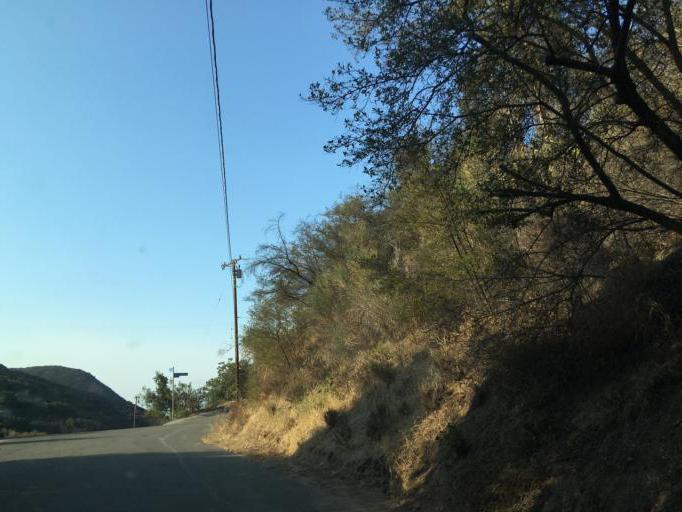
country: US
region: California
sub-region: Los Angeles County
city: Las Flores
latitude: 34.0586
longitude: -118.6378
